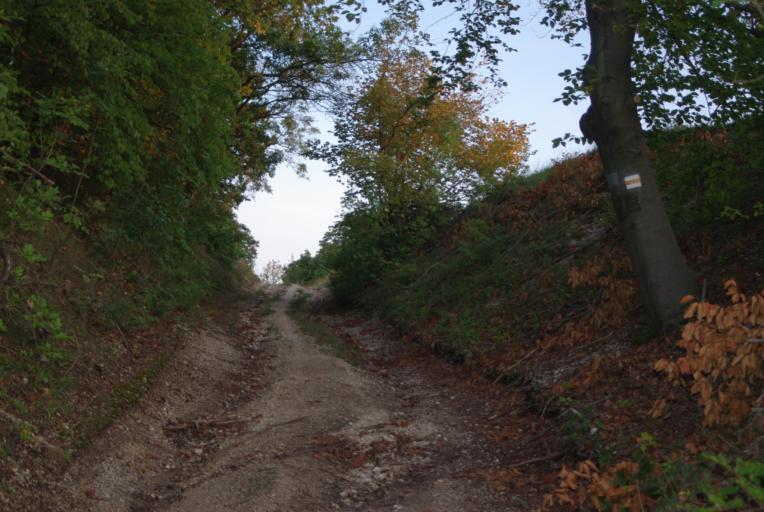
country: HU
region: Pest
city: Telki
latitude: 47.5899
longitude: 18.8348
